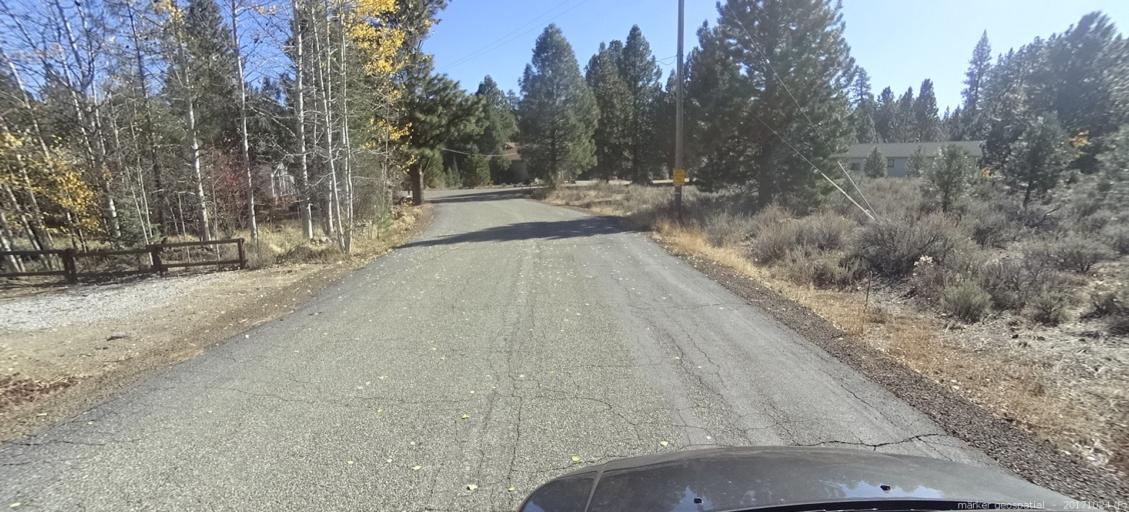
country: US
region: California
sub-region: Shasta County
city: Burney
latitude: 40.6552
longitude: -121.4634
